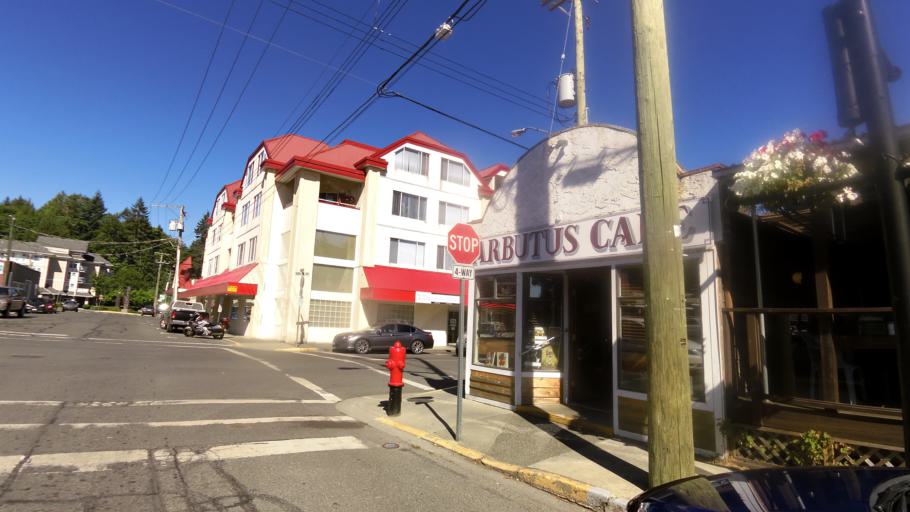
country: CA
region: British Columbia
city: Duncan
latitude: 48.7785
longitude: -123.7103
